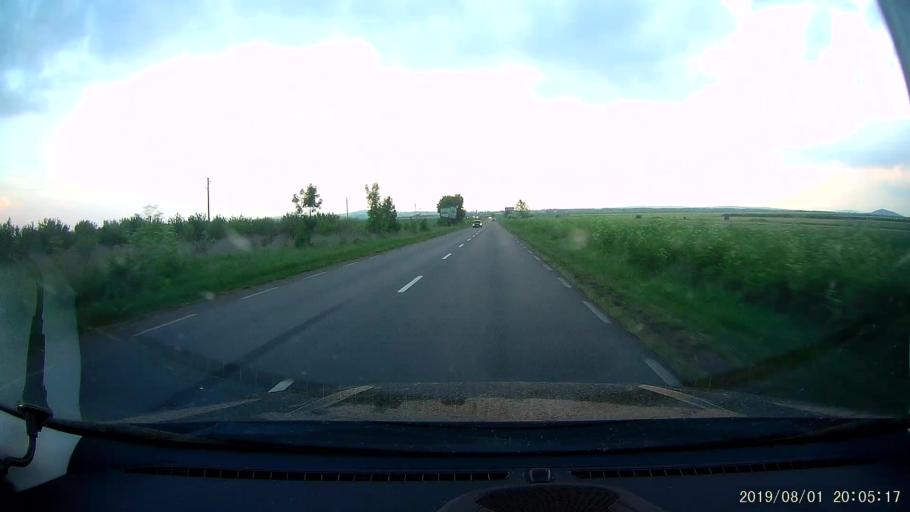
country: BG
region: Yambol
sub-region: Obshtina Yambol
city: Yambol
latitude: 42.5482
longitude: 26.5693
